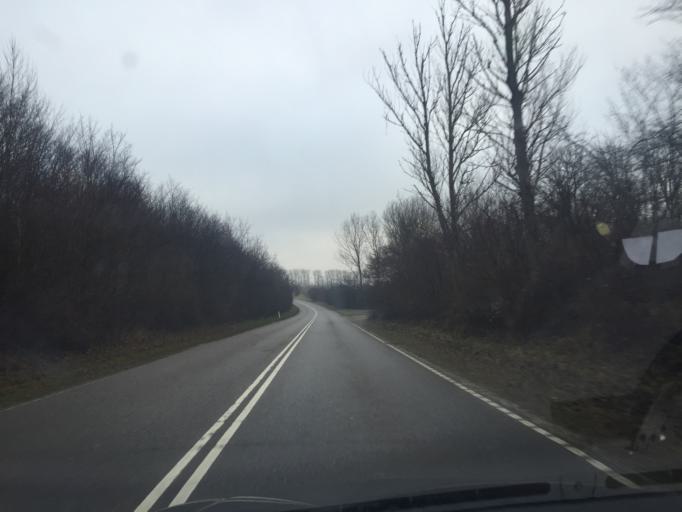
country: DK
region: Capital Region
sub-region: Hoje-Taastrup Kommune
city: Flong
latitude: 55.6786
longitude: 12.2389
